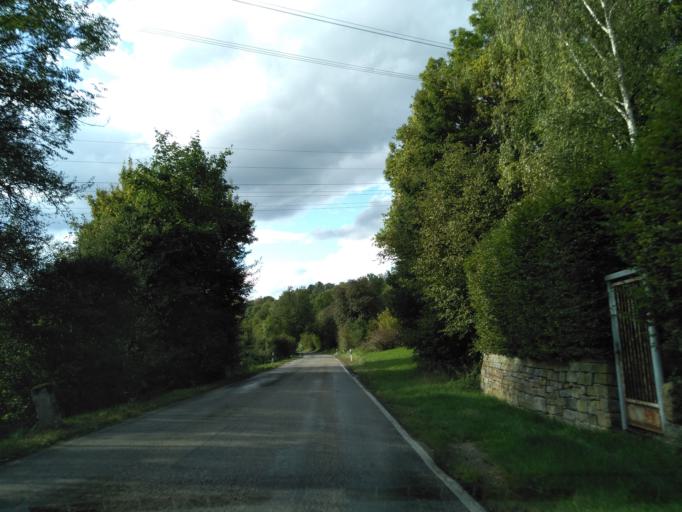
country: DE
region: Baden-Wuerttemberg
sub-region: Regierungsbezirk Stuttgart
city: Markgroningen
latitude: 48.9397
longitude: 9.0702
